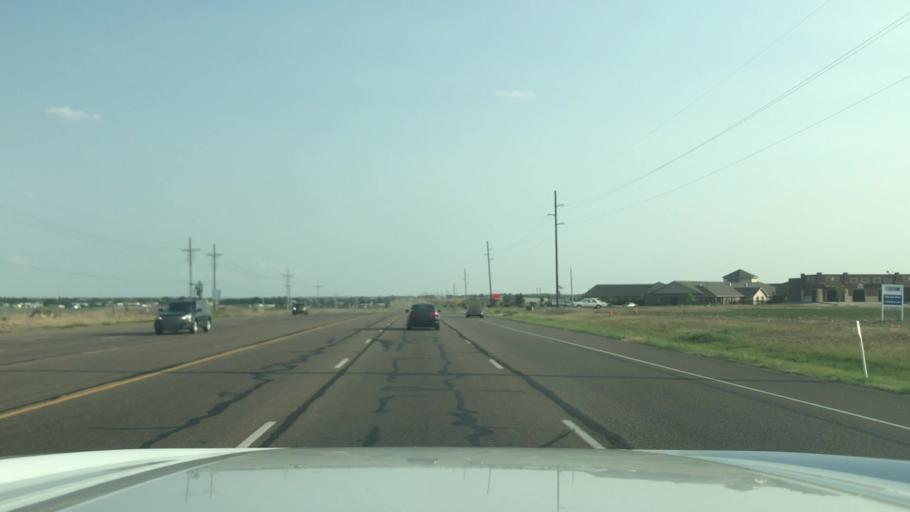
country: US
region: Texas
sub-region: Potter County
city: Amarillo
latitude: 35.1421
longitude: -101.9382
